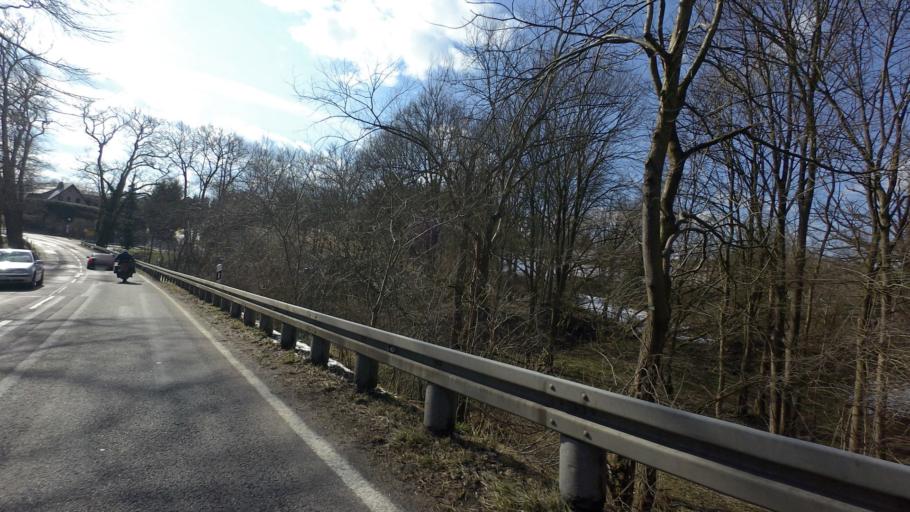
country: DE
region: Brandenburg
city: Rudnitz
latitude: 52.7619
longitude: 13.5705
